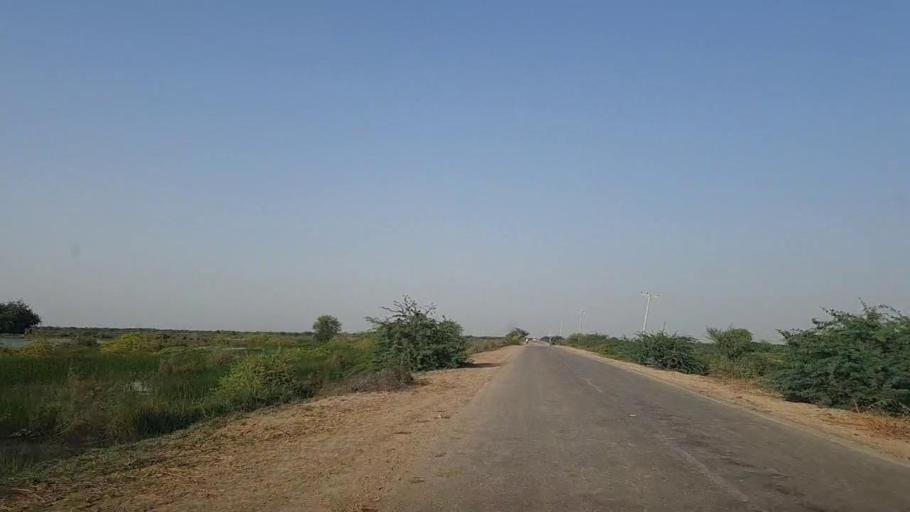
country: PK
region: Sindh
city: Mirpur Batoro
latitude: 24.6006
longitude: 68.4007
